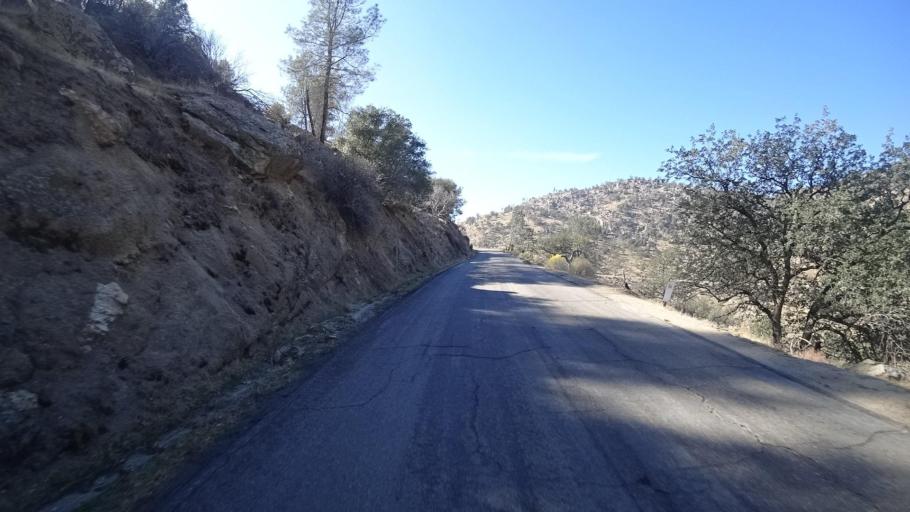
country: US
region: California
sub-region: Kern County
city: Bodfish
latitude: 35.5643
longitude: -118.5816
